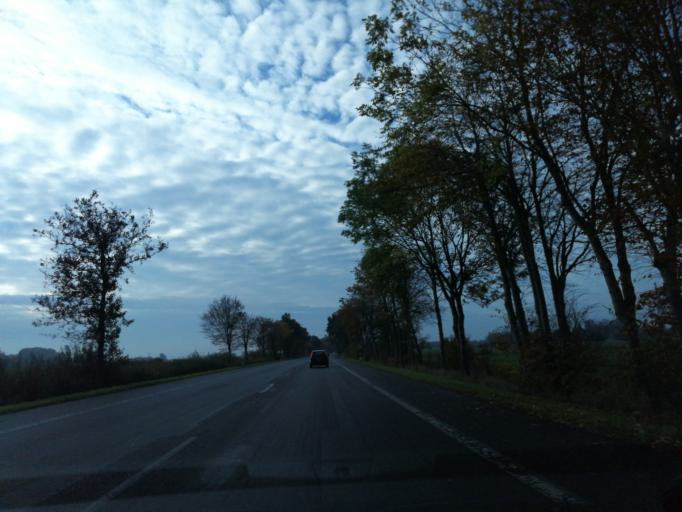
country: DE
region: Lower Saxony
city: Fedderwarden
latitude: 53.5728
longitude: 8.0564
